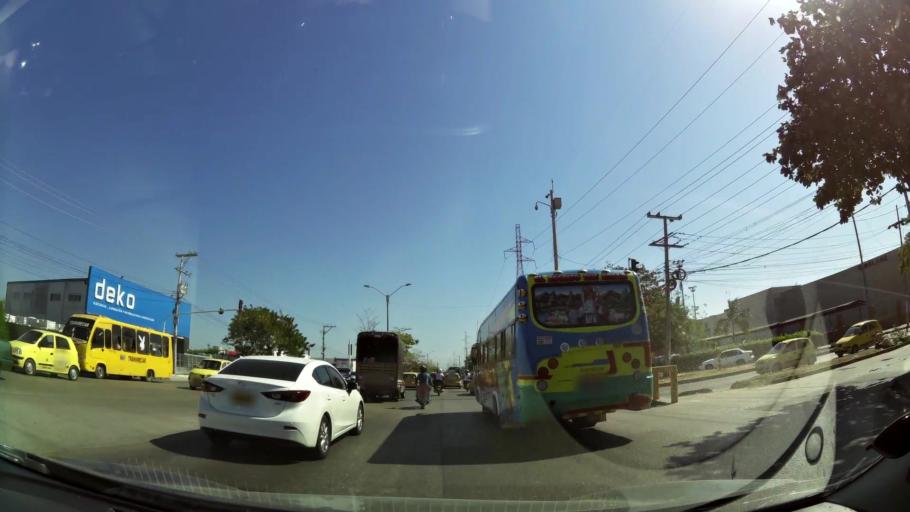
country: CO
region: Atlantico
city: Barranquilla
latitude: 10.9470
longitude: -74.7849
